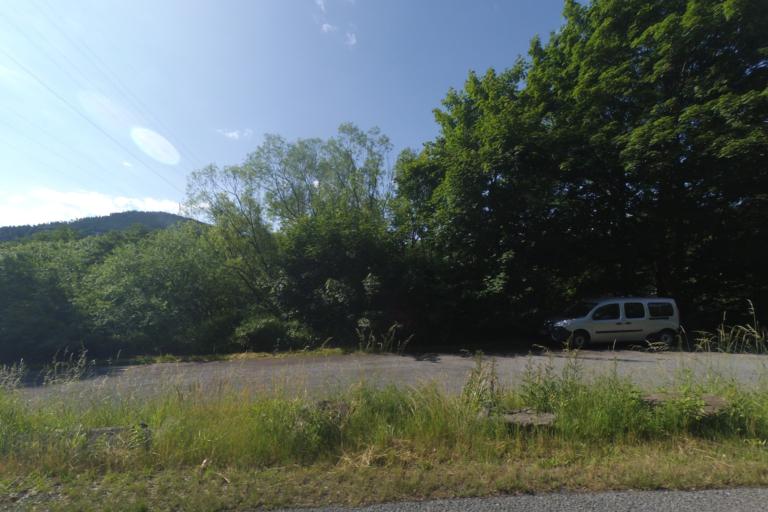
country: DE
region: Thuringia
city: Kaulsdorf
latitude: 50.6145
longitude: 11.4404
